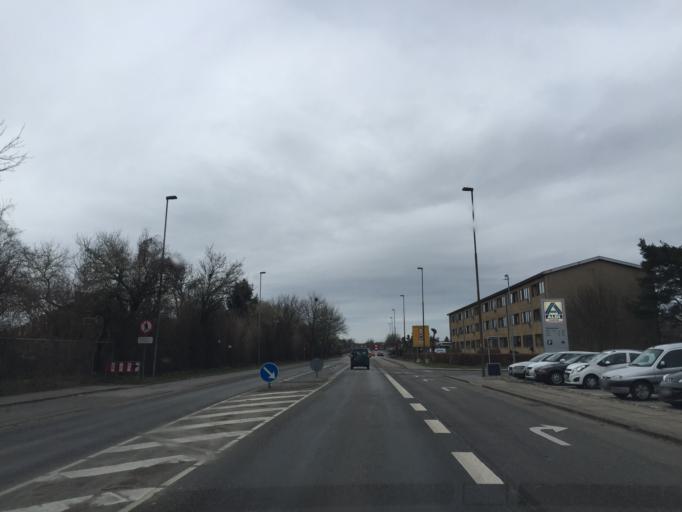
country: DK
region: South Denmark
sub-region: Odense Kommune
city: Odense
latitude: 55.4043
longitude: 10.3401
